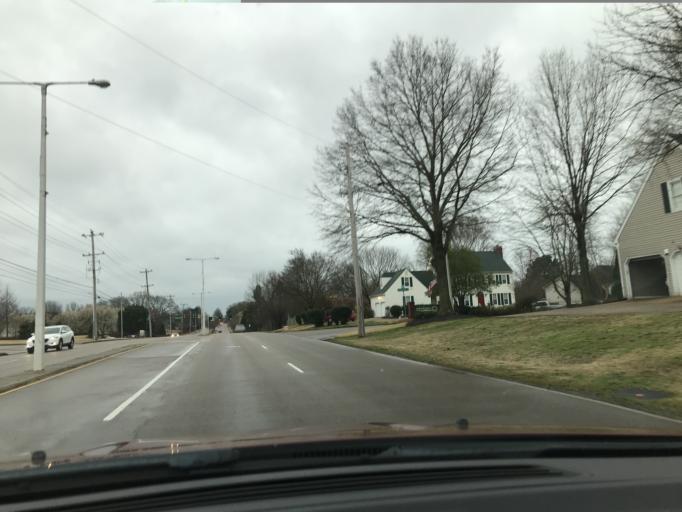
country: US
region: Tennessee
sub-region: Shelby County
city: Collierville
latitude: 35.0631
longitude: -89.6859
